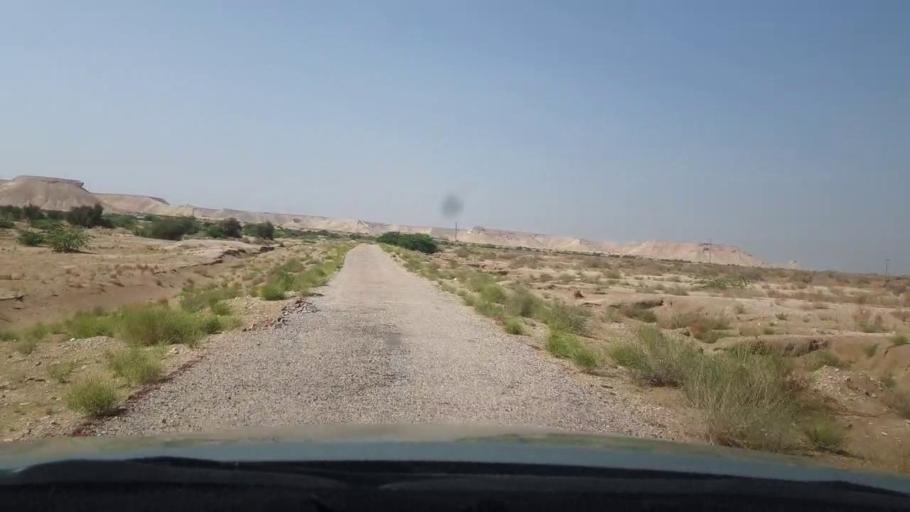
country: PK
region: Sindh
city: Kot Diji
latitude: 27.3312
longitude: 68.8161
